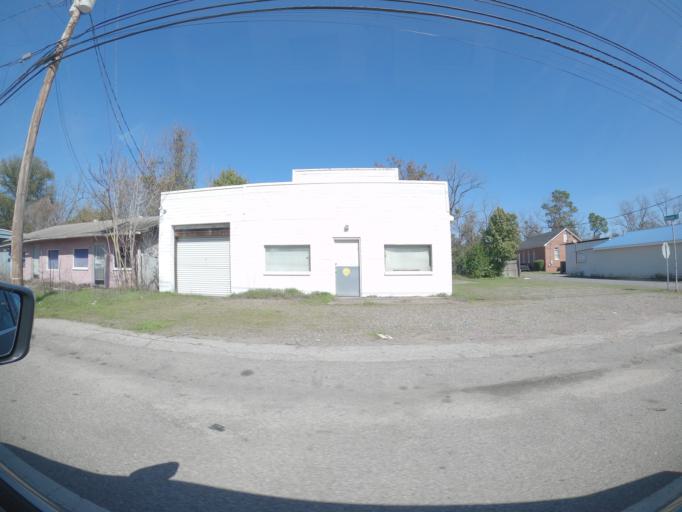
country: US
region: South Carolina
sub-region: Aiken County
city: North Augusta
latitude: 33.4851
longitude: -81.9474
